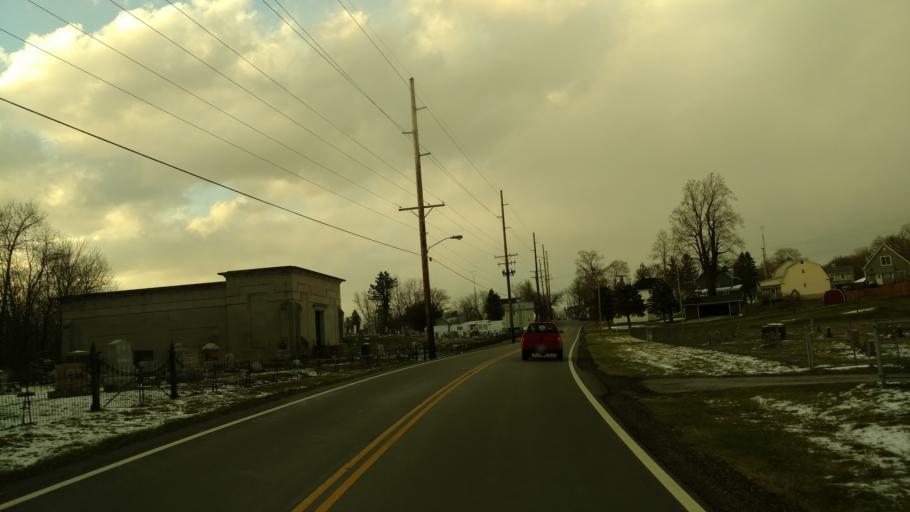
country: US
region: Ohio
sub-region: Ashland County
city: Ashland
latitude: 40.8003
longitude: -82.1941
